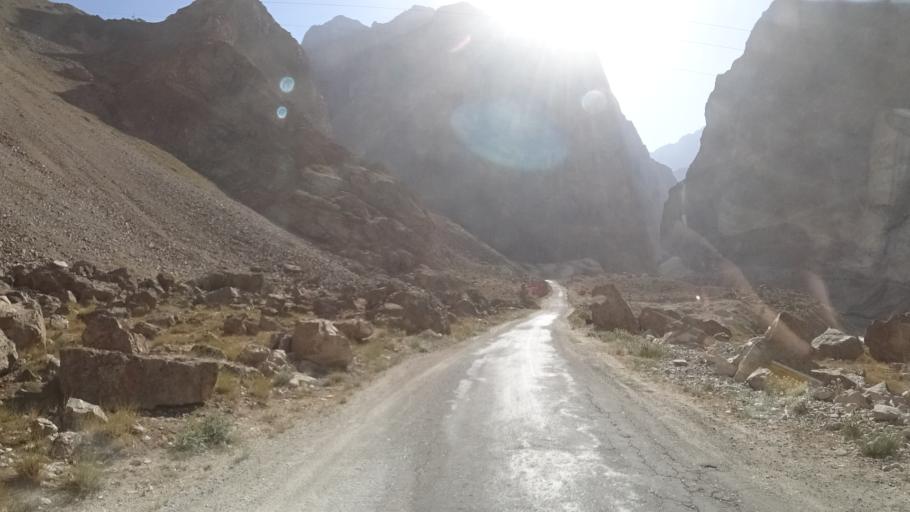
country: TJ
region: Gorno-Badakhshan
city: Rushon
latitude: 37.9936
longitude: 71.2777
